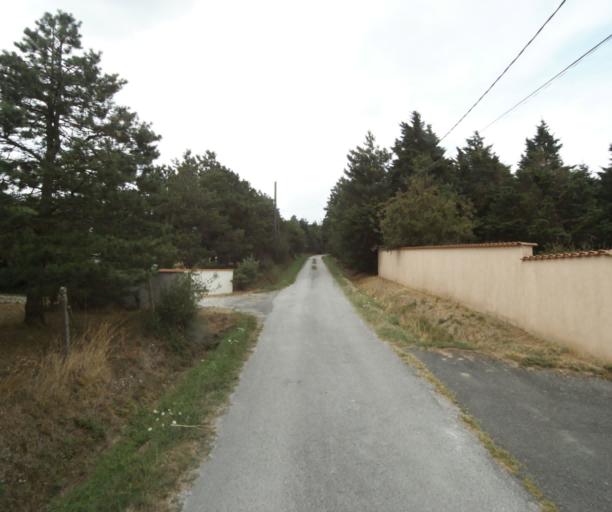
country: FR
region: Midi-Pyrenees
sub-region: Departement de la Haute-Garonne
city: Revel
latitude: 43.4376
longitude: 2.0136
